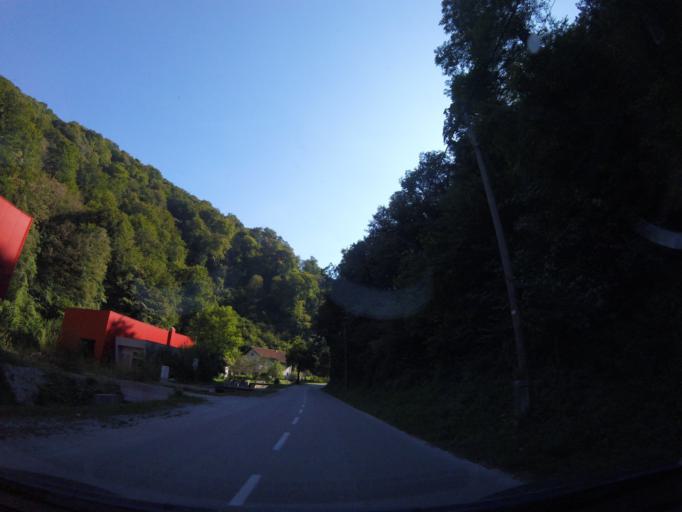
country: HR
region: Zagrebacka
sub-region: Grad Samobor
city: Samobor
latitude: 45.7970
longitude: 15.6932
